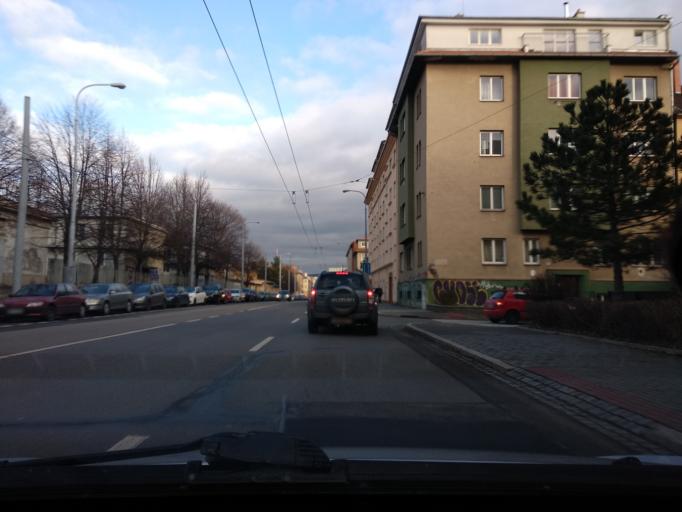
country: CZ
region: South Moravian
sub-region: Mesto Brno
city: Brno
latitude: 49.2132
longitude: 16.6193
